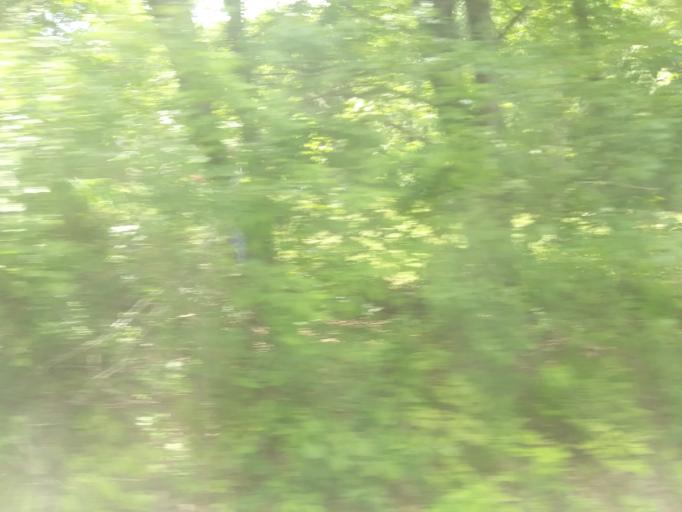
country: US
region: Massachusetts
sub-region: Franklin County
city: Shelburne Falls
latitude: 42.5920
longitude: -72.7462
